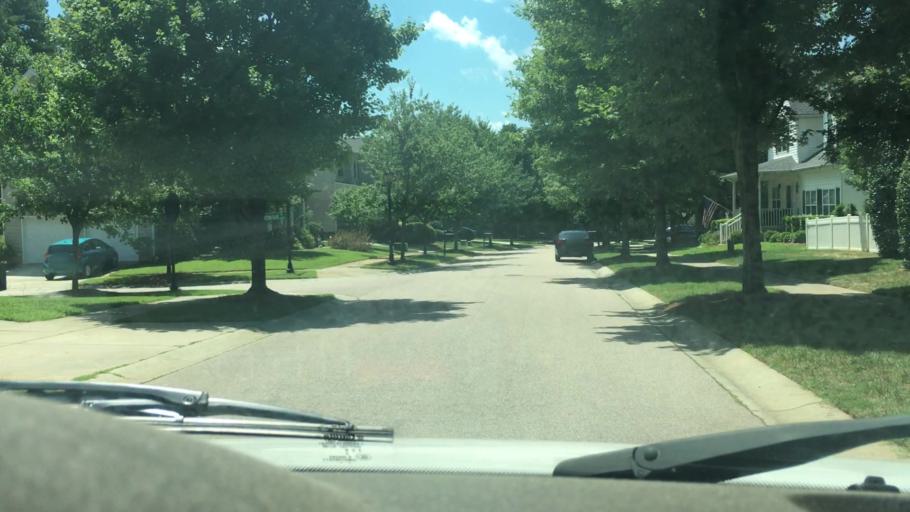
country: US
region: North Carolina
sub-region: Mecklenburg County
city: Cornelius
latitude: 35.4633
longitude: -80.8608
